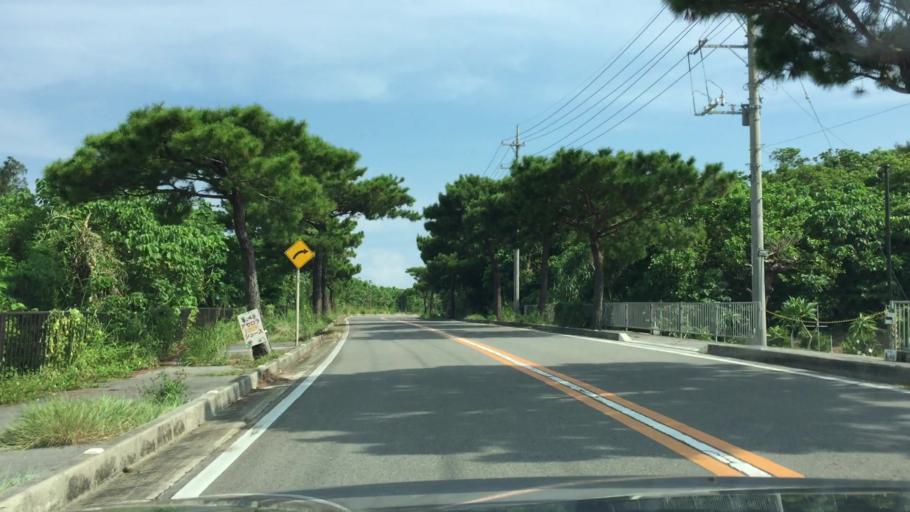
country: JP
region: Okinawa
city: Ishigaki
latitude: 24.4917
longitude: 124.2796
